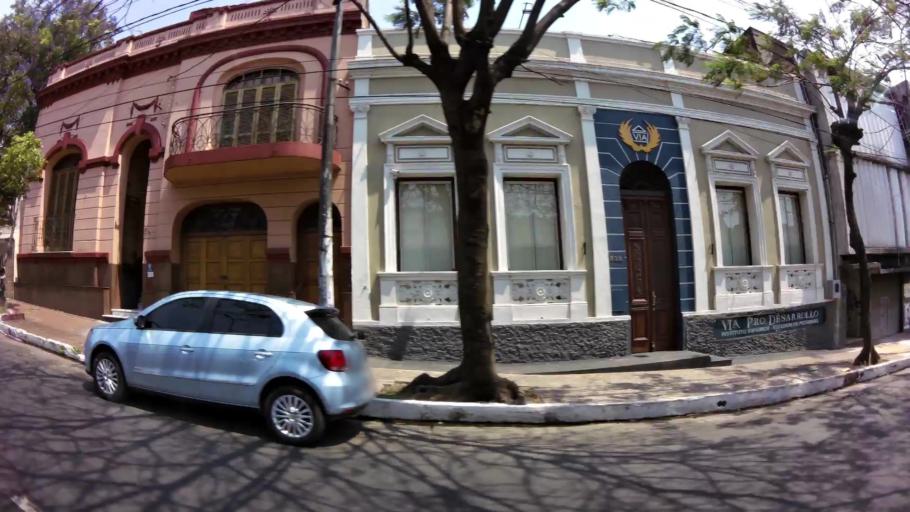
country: PY
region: Asuncion
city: Asuncion
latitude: -25.2824
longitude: -57.6443
